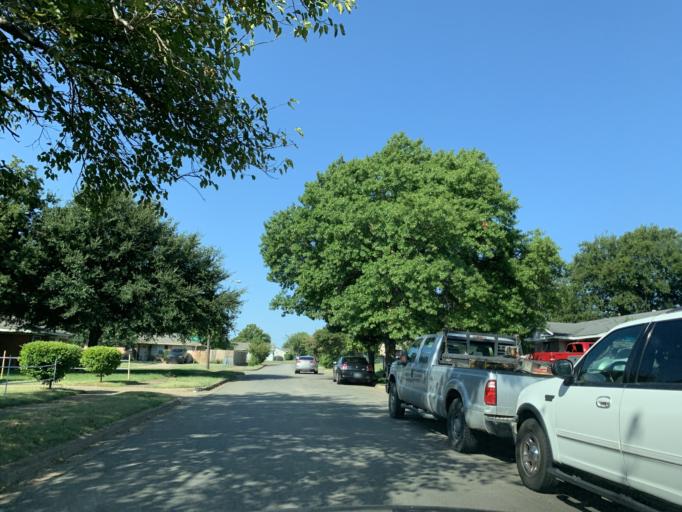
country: US
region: Texas
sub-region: Dallas County
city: Hutchins
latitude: 32.6656
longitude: -96.7602
